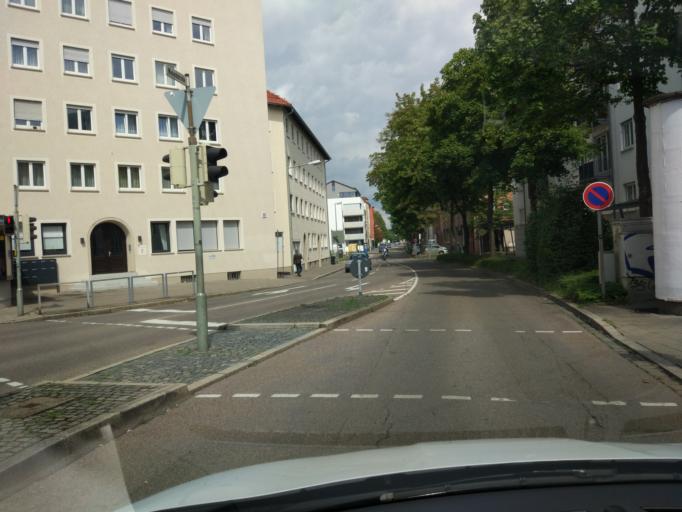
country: DE
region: Baden-Wuerttemberg
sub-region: Tuebingen Region
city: Ulm
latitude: 48.4034
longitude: 9.9998
